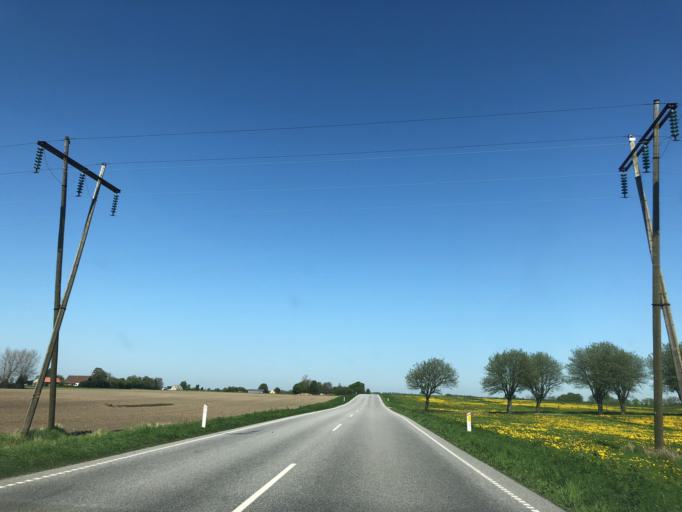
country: DK
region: Zealand
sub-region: Slagelse Kommune
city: Skaelskor
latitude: 55.3047
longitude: 11.2895
